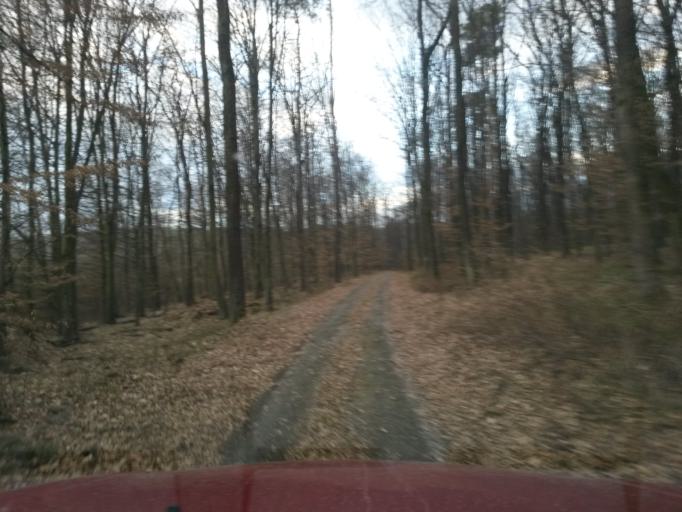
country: SK
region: Kosicky
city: Kosice
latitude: 48.6954
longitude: 21.3028
